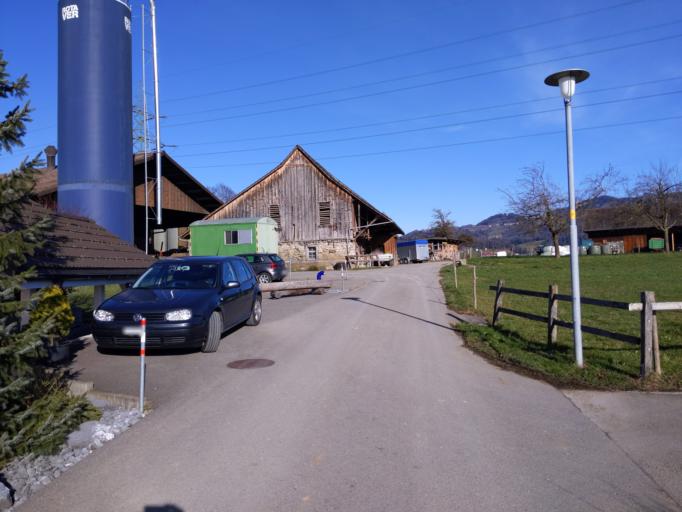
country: CH
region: Saint Gallen
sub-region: Wahlkreis See-Gaster
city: Schmerikon
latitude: 47.2308
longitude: 8.9414
